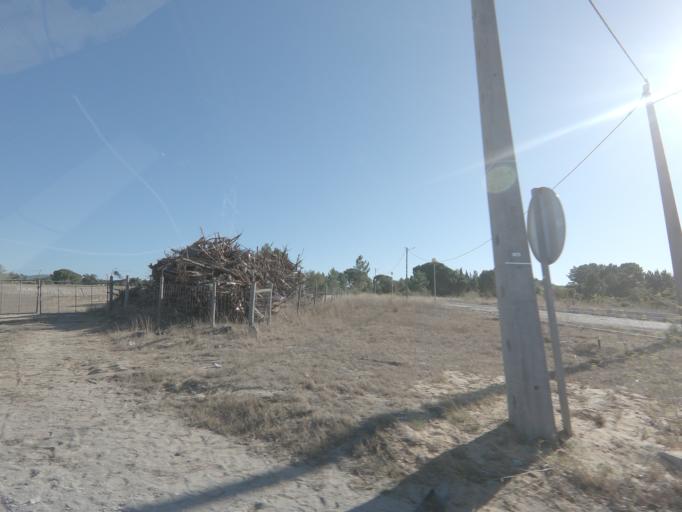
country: PT
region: Setubal
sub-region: Palmela
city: Pinhal Novo
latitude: 38.6138
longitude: -8.9508
